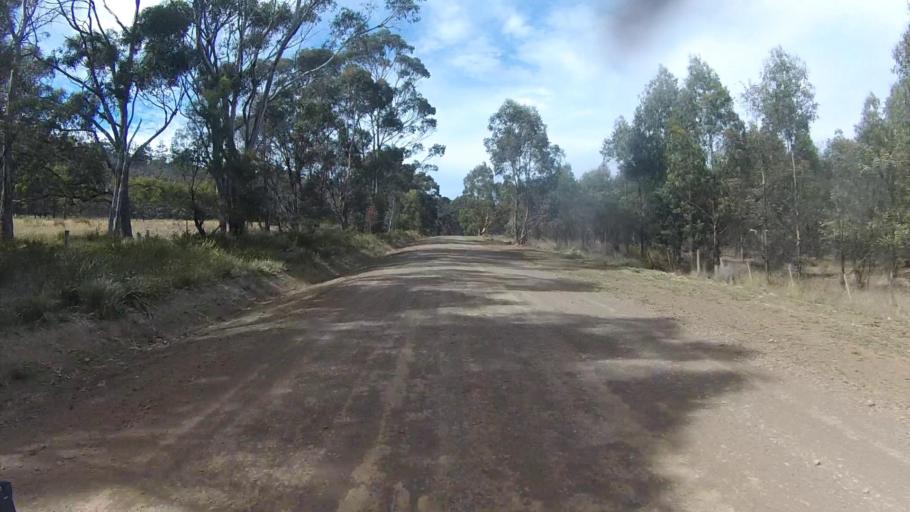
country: AU
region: Tasmania
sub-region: Sorell
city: Sorell
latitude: -42.6541
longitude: 147.8981
